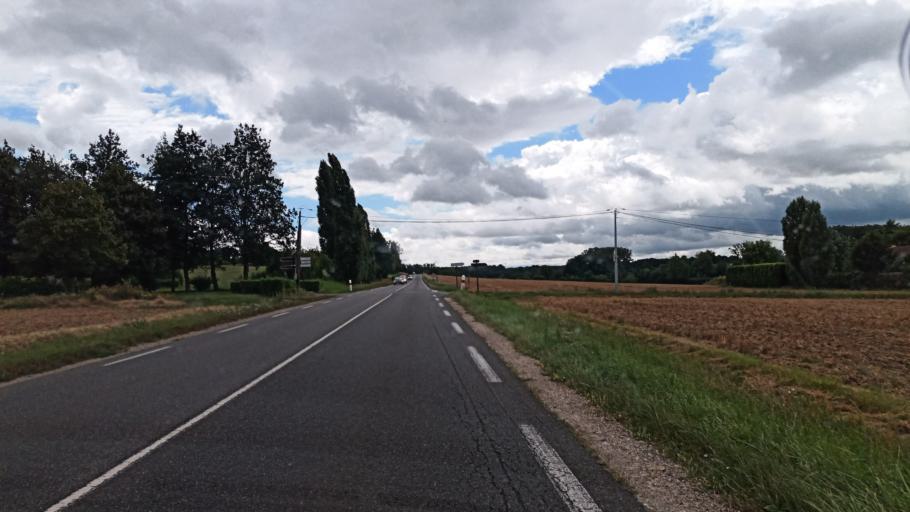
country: FR
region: Ile-de-France
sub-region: Departement de Seine-et-Marne
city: Voulx
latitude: 48.3003
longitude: 2.9477
